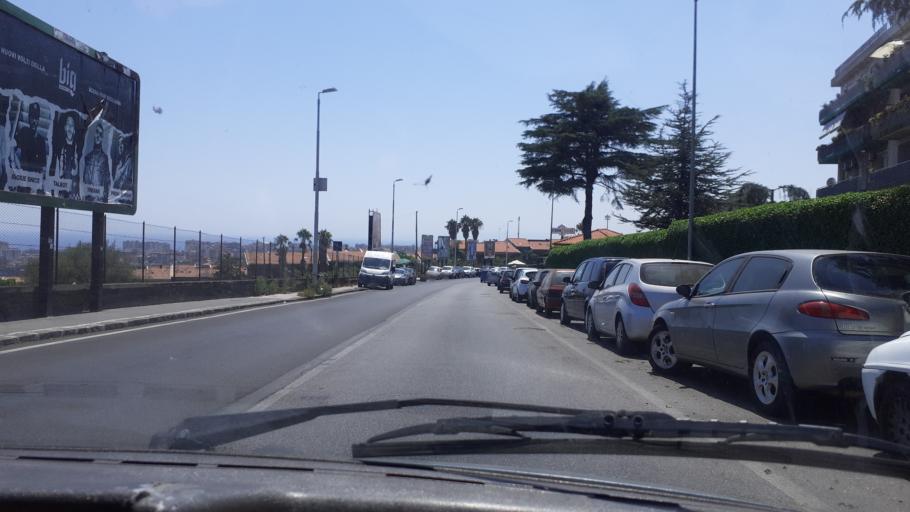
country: IT
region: Sicily
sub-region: Catania
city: Cerza
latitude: 37.5388
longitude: 15.1025
